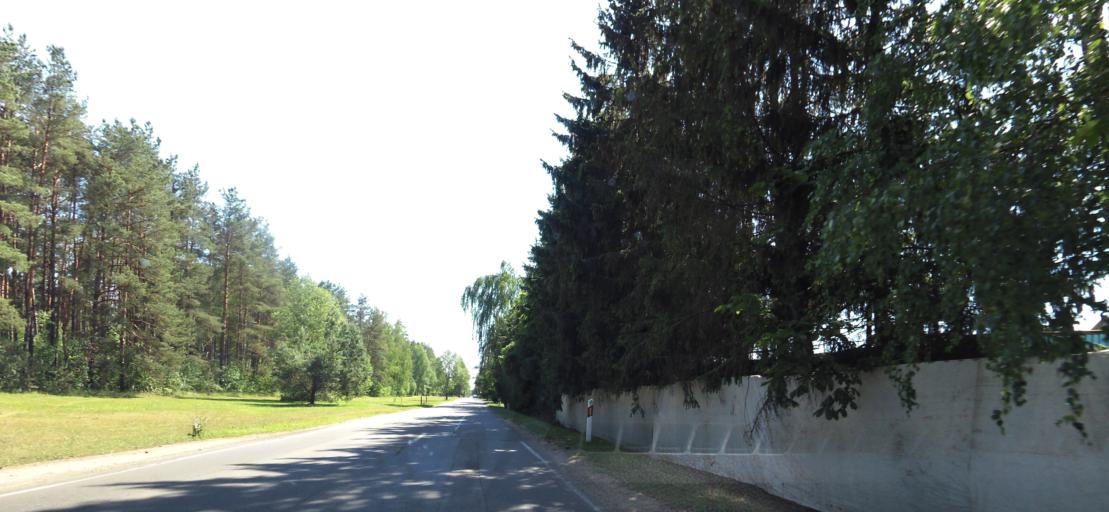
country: LT
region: Vilnius County
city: Rasos
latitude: 54.7893
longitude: 25.3505
